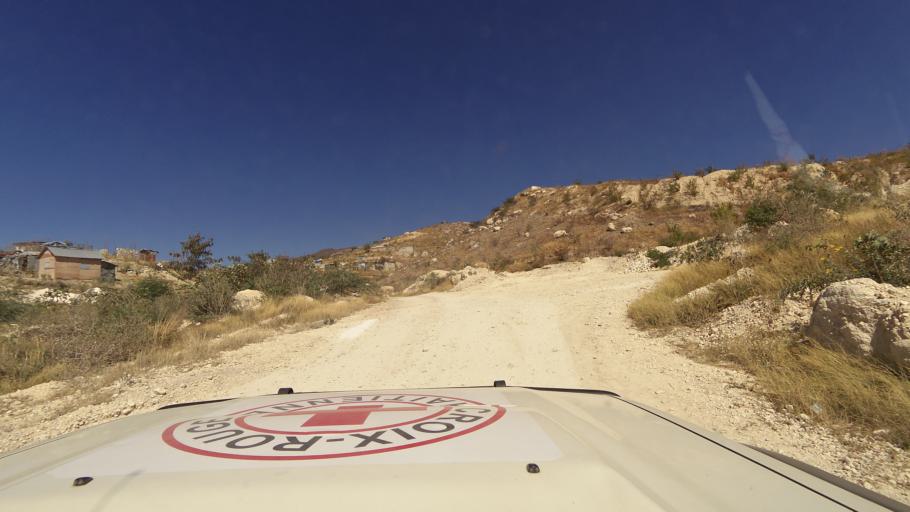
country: HT
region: Ouest
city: Croix des Bouquets
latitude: 18.6683
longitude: -72.2771
